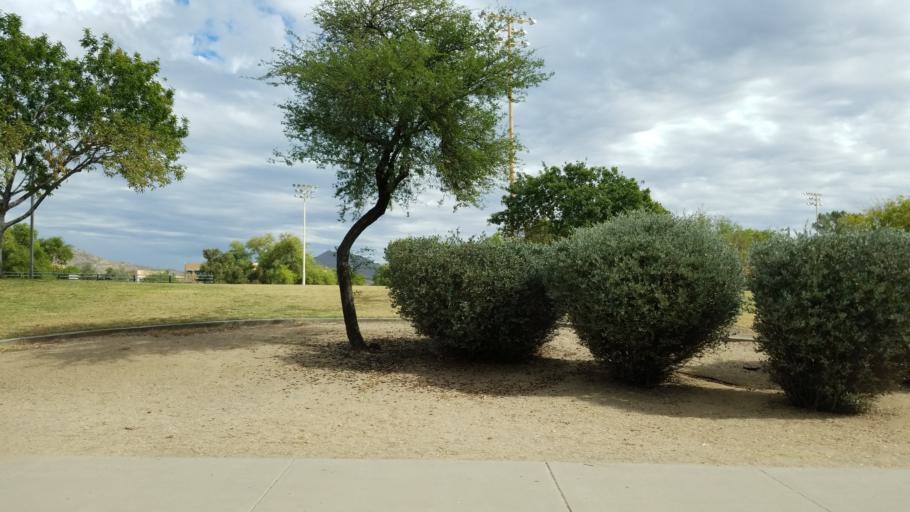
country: US
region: Arizona
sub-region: Maricopa County
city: Glendale
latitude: 33.5788
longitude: -112.1135
